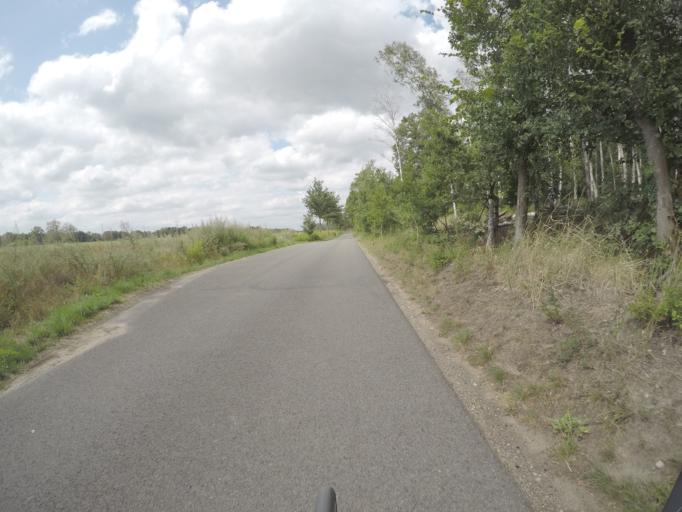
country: DE
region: Brandenburg
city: Falkensee
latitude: 52.6042
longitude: 13.0870
